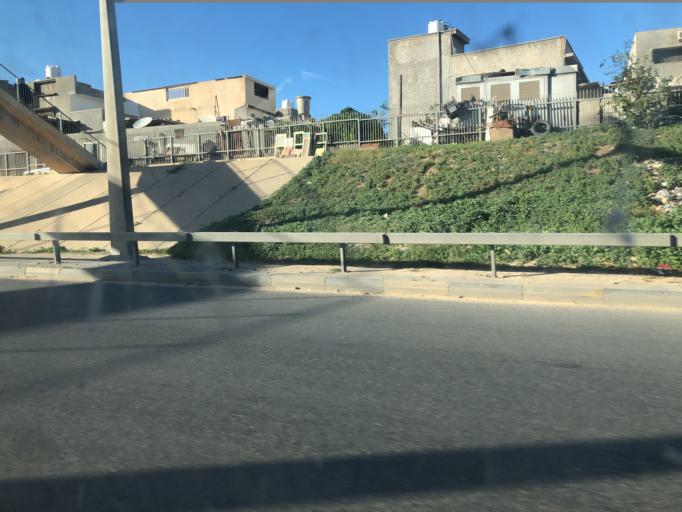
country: LY
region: Tripoli
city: Tripoli
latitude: 32.8689
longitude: 13.2407
